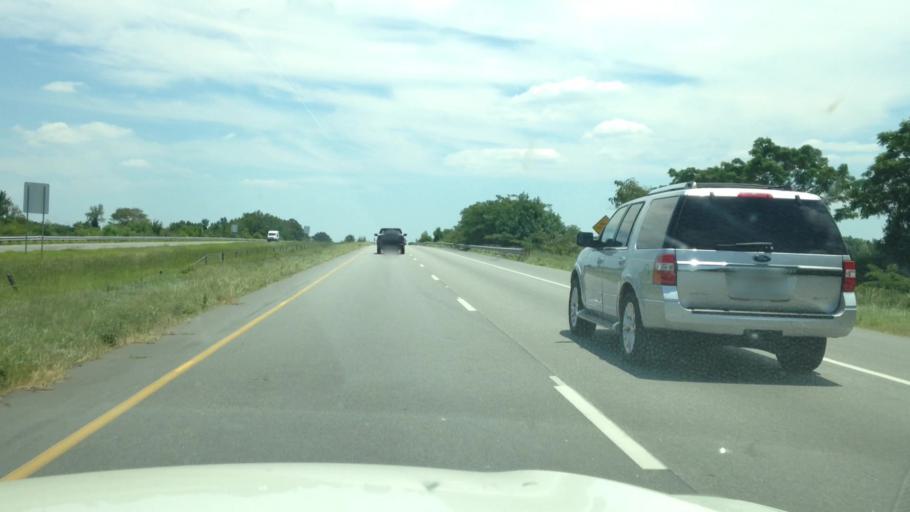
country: US
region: South Carolina
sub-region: Lee County
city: Bishopville
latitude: 34.1915
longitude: -80.2609
